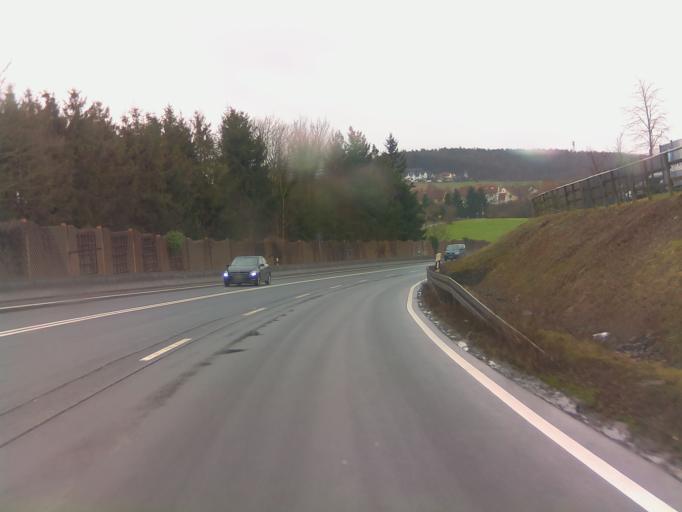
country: DE
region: Hesse
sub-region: Regierungsbezirk Kassel
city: Kunzell
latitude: 50.5364
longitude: 9.6989
